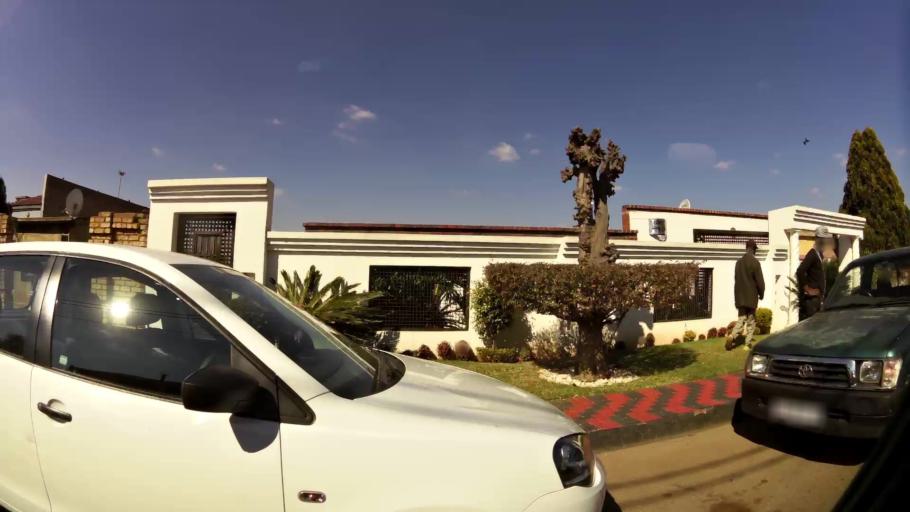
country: ZA
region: Gauteng
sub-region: City of Johannesburg Metropolitan Municipality
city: Soweto
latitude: -26.2454
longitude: 27.8972
